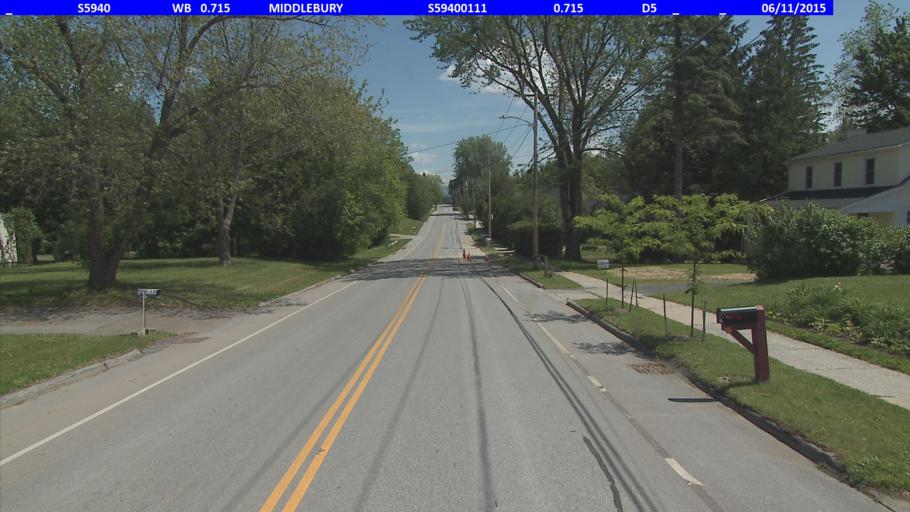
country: US
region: Vermont
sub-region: Addison County
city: Middlebury (village)
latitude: 44.0189
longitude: -73.1811
